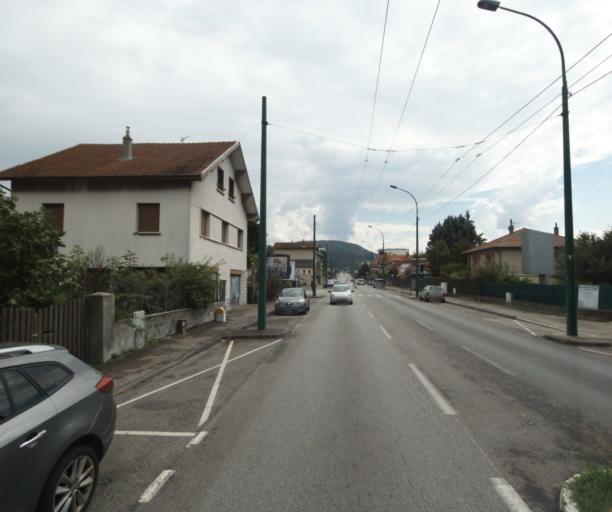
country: FR
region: Rhone-Alpes
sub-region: Departement de l'Isere
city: Eybens
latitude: 45.1602
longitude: 5.7451
